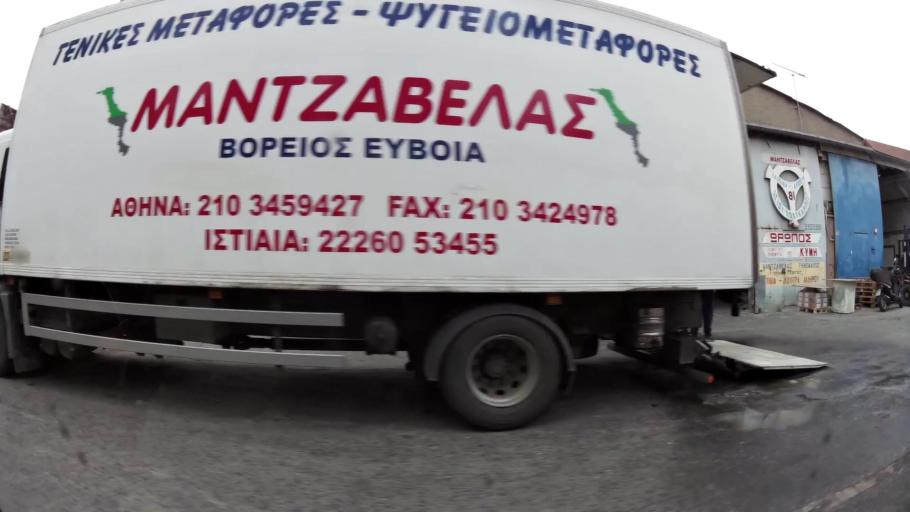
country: GR
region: Attica
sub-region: Nomarchia Athinas
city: Tavros
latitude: 37.9828
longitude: 23.6996
